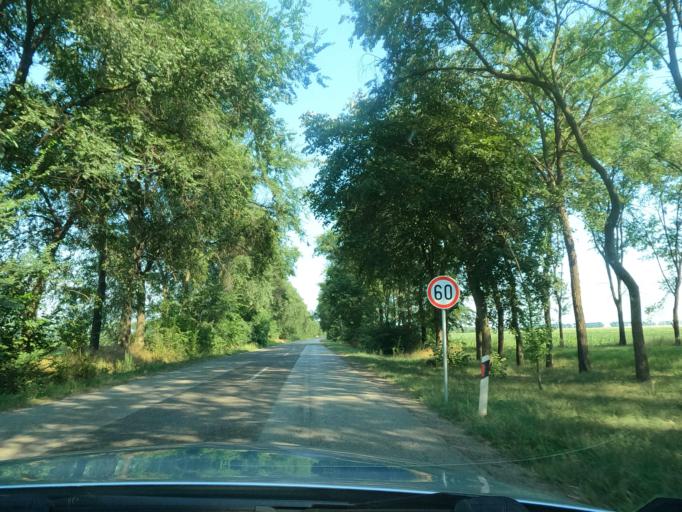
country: RS
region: Autonomna Pokrajina Vojvodina
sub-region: Juznobacki Okrug
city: Becej
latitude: 45.6669
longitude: 19.9340
